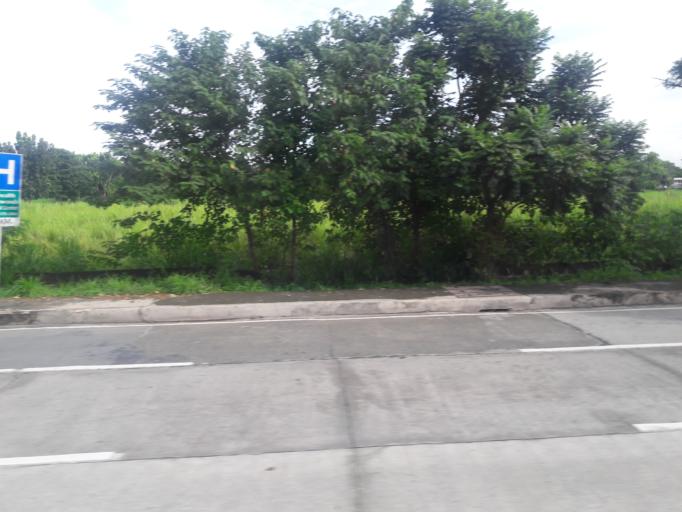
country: PH
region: Calabarzon
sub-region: Province of Cavite
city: Carmona
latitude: 14.3139
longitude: 121.0494
